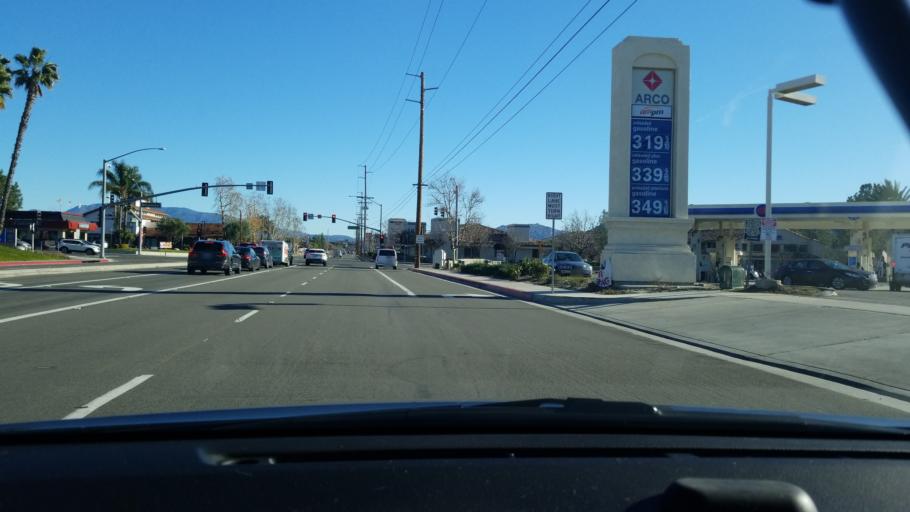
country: US
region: California
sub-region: Riverside County
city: Temecula
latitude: 33.5215
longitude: -117.1658
